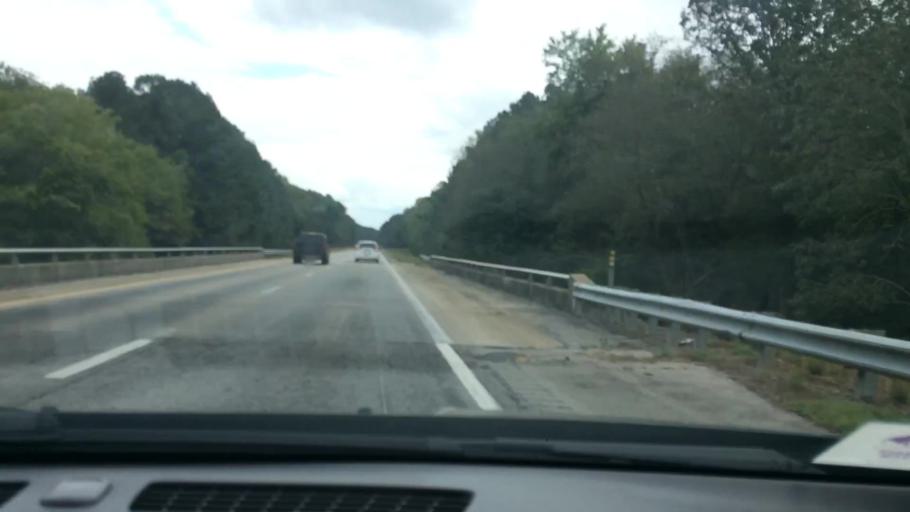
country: US
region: North Carolina
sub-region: Wake County
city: Zebulon
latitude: 35.7948
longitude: -78.1700
